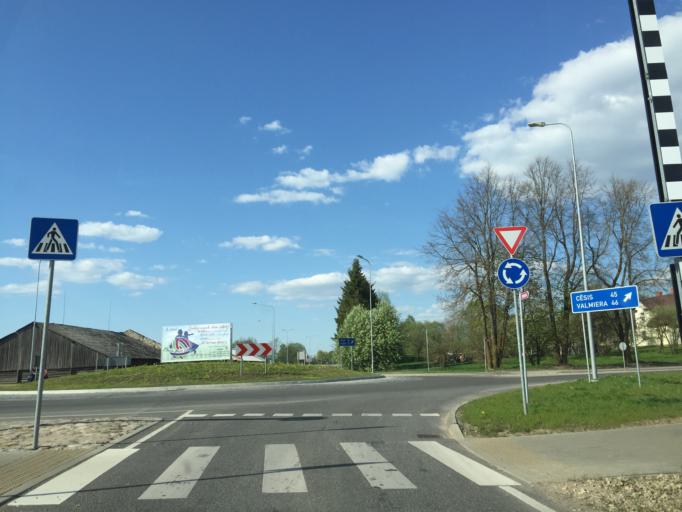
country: LV
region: Limbazu Rajons
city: Limbazi
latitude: 57.5127
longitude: 24.7240
